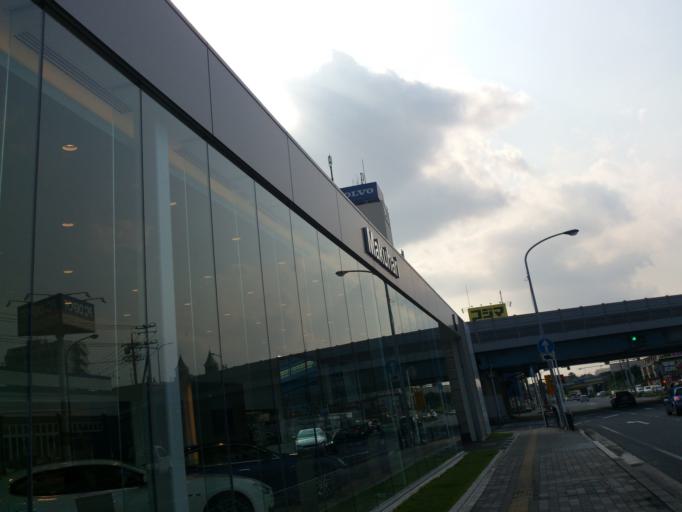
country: JP
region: Chiba
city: Funabashi
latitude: 35.6669
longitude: 140.0384
